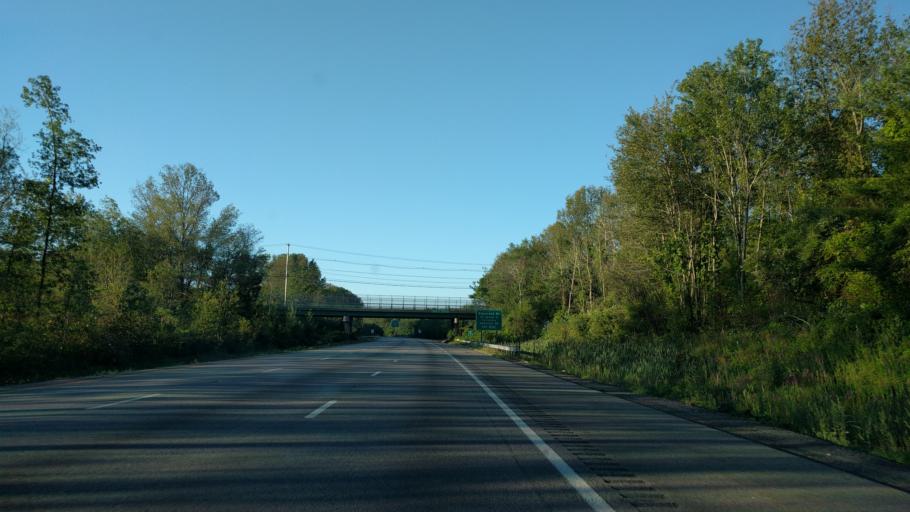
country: US
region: Massachusetts
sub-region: Middlesex County
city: Marlborough
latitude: 42.3342
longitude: -71.5759
